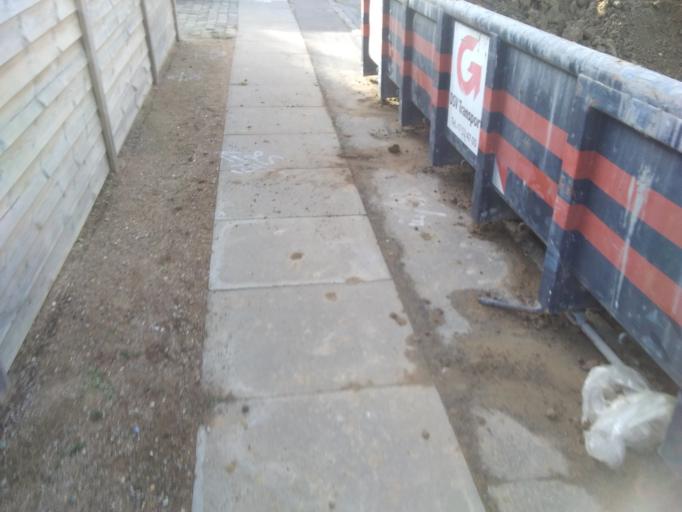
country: DK
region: Capital Region
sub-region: Kobenhavn
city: Vanlose
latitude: 55.6982
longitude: 12.4940
